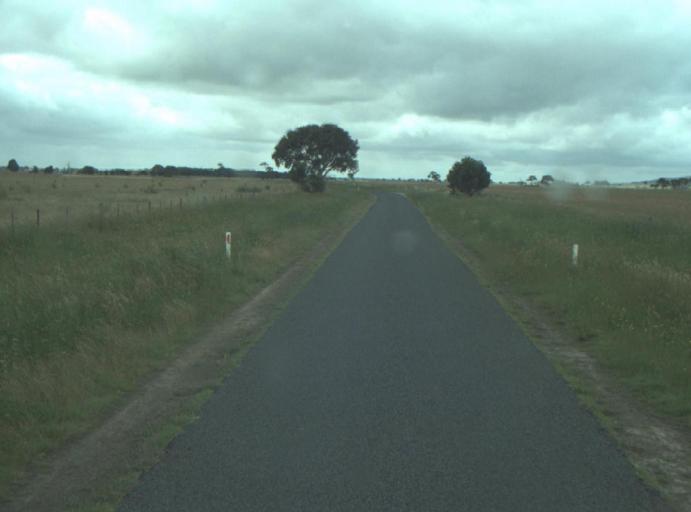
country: AU
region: Victoria
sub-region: Greater Geelong
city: Lara
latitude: -37.8486
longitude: 144.3544
